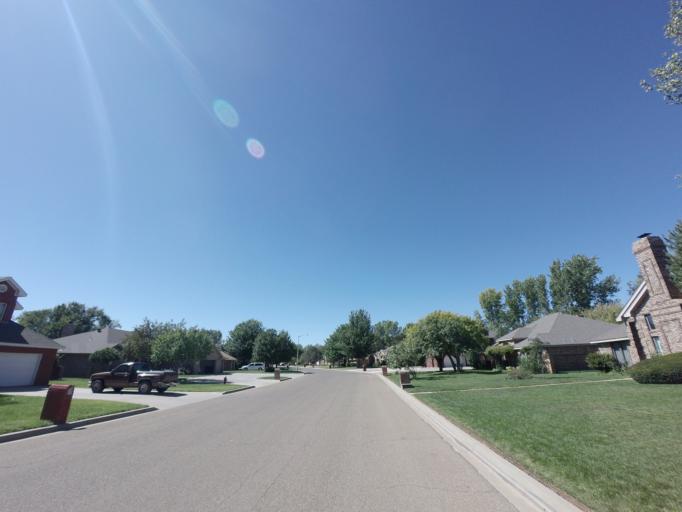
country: US
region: New Mexico
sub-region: Curry County
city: Clovis
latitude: 34.4430
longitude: -103.1845
